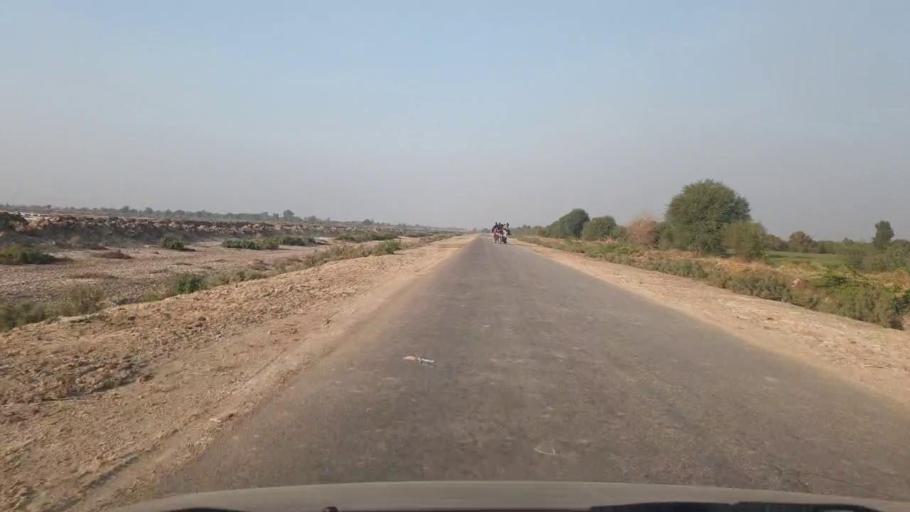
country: PK
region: Sindh
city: Mirwah Gorchani
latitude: 25.3575
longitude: 69.1747
